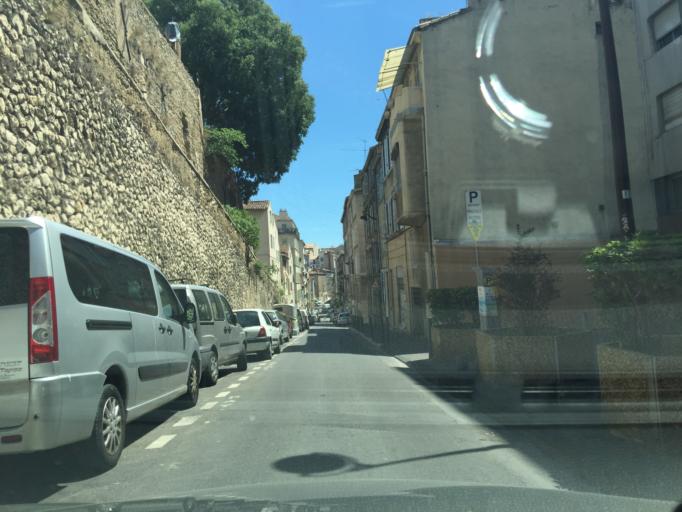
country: FR
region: Provence-Alpes-Cote d'Azur
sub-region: Departement des Bouches-du-Rhone
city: Marseille 01
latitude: 43.3038
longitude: 5.3891
